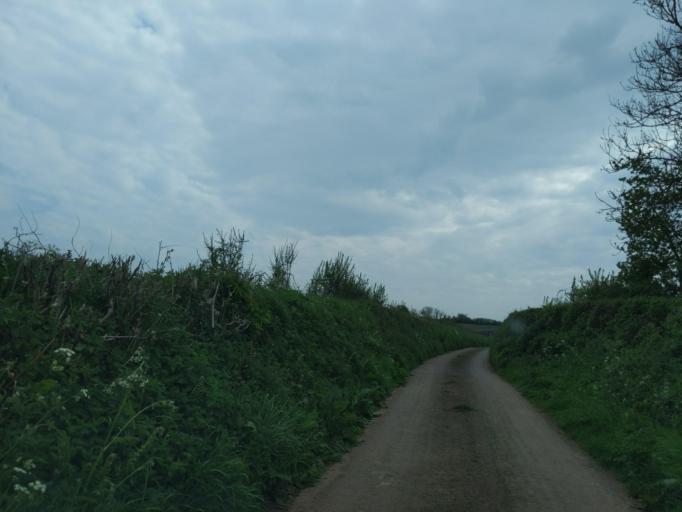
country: GB
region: England
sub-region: Devon
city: Yealmpton
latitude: 50.3647
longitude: -4.0244
